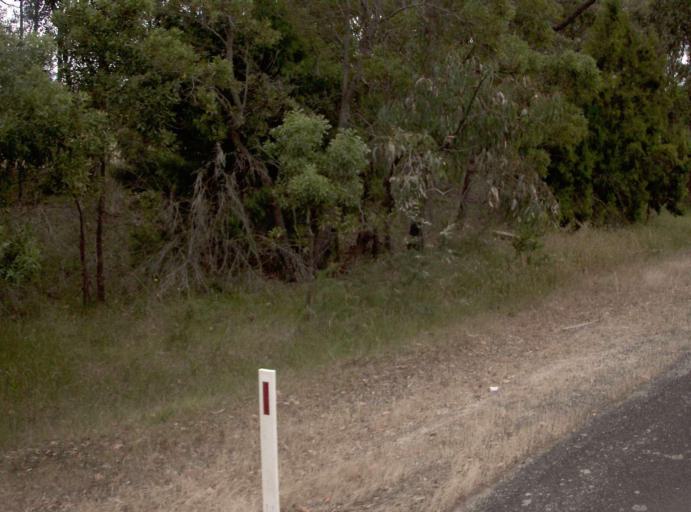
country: AU
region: Victoria
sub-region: Wellington
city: Sale
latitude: -38.3515
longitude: 146.9977
